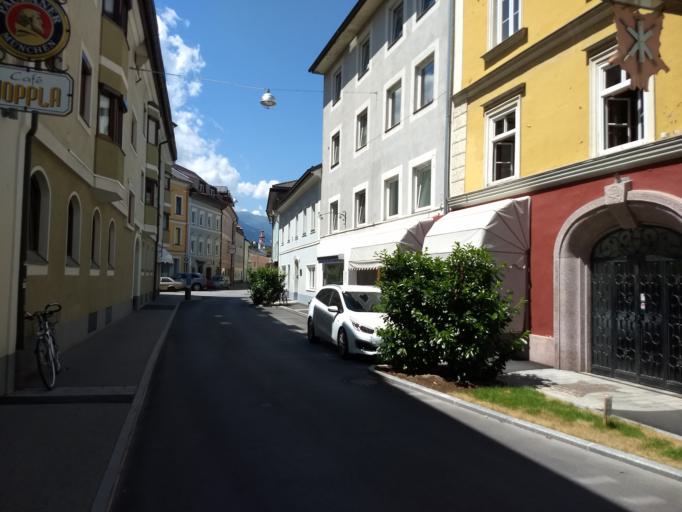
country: AT
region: Tyrol
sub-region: Politischer Bezirk Lienz
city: Lienz
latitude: 46.8308
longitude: 12.7638
